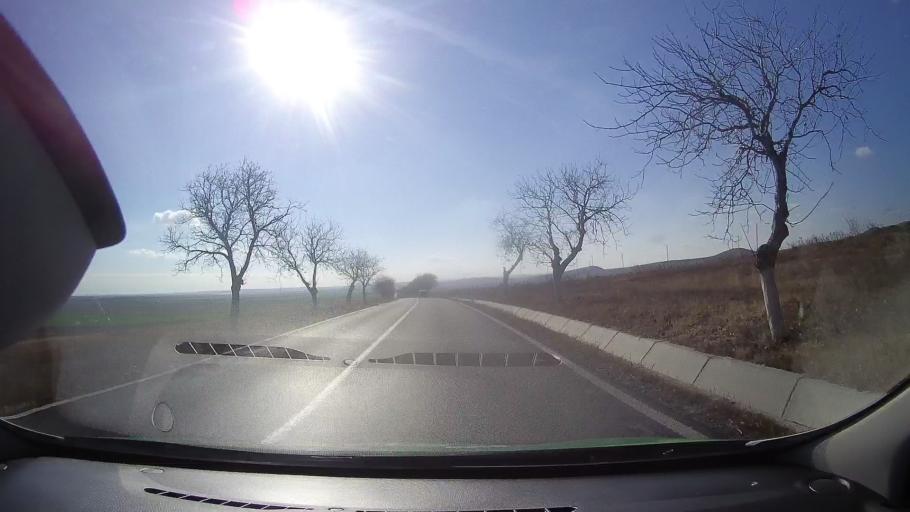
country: RO
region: Tulcea
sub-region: Comuna Ceamurlia de Jos
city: Ceamurlia de Jos
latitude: 44.8070
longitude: 28.6910
